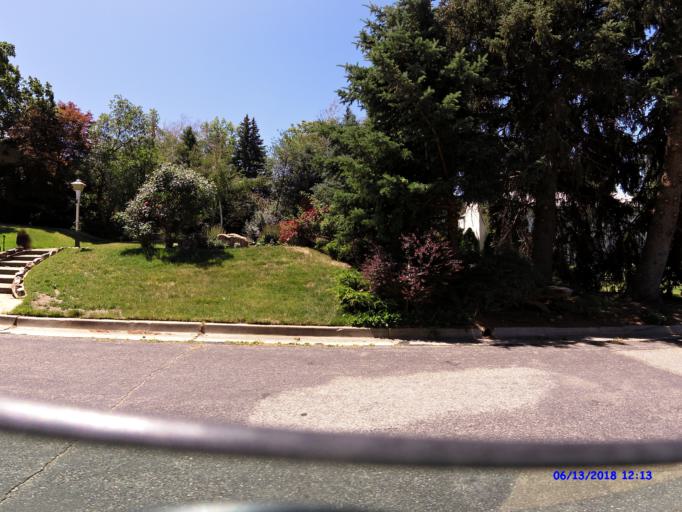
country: US
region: Utah
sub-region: Weber County
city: Ogden
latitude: 41.2144
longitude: -111.9352
